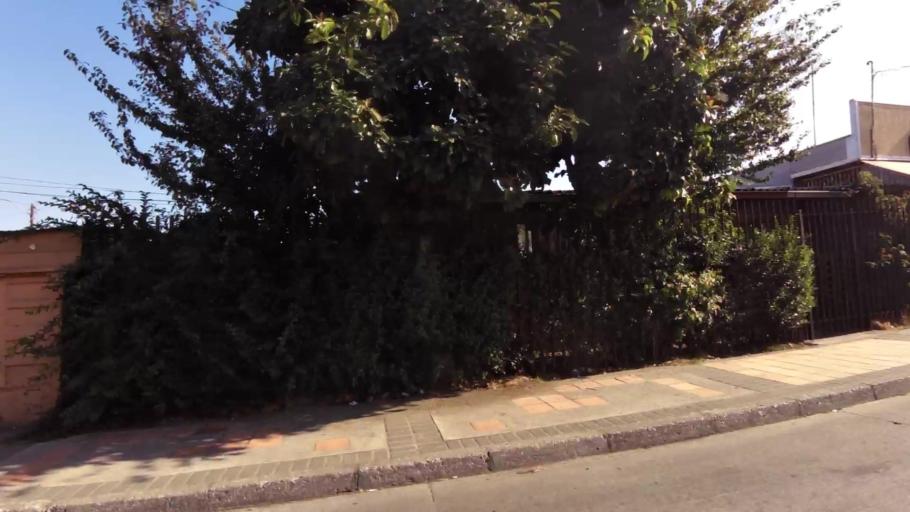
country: CL
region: Biobio
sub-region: Provincia de Concepcion
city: Concepcion
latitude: -36.7959
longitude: -73.0931
